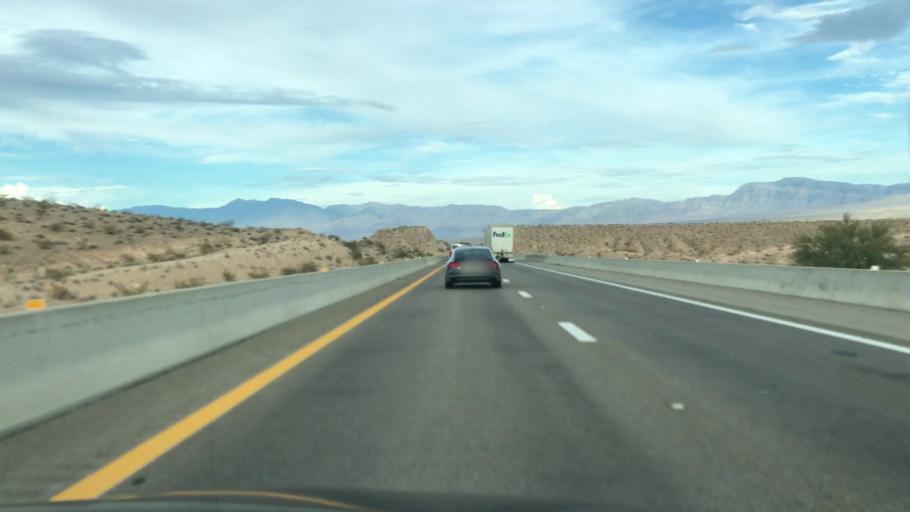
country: US
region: Nevada
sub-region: Clark County
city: Bunkerville
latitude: 36.7677
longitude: -114.2147
